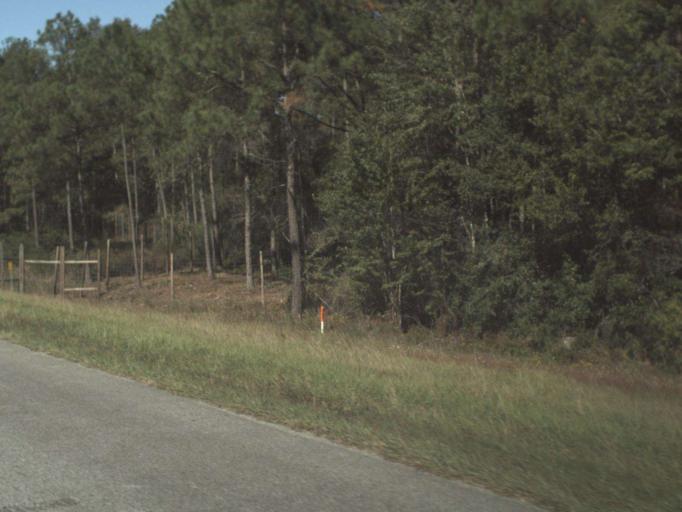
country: US
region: Florida
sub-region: Washington County
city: Chipley
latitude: 30.7530
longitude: -85.5915
